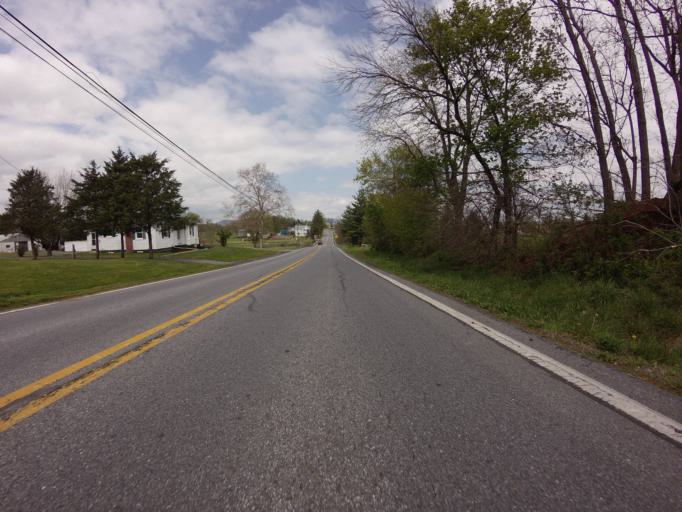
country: US
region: Maryland
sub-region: Frederick County
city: Thurmont
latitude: 39.5778
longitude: -77.3652
